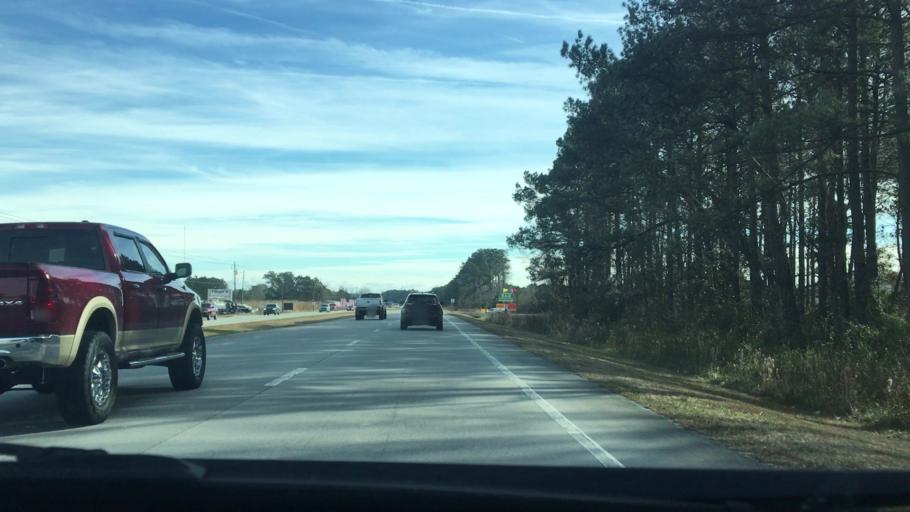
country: US
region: North Carolina
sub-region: Carteret County
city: Newport
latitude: 34.7568
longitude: -76.8482
